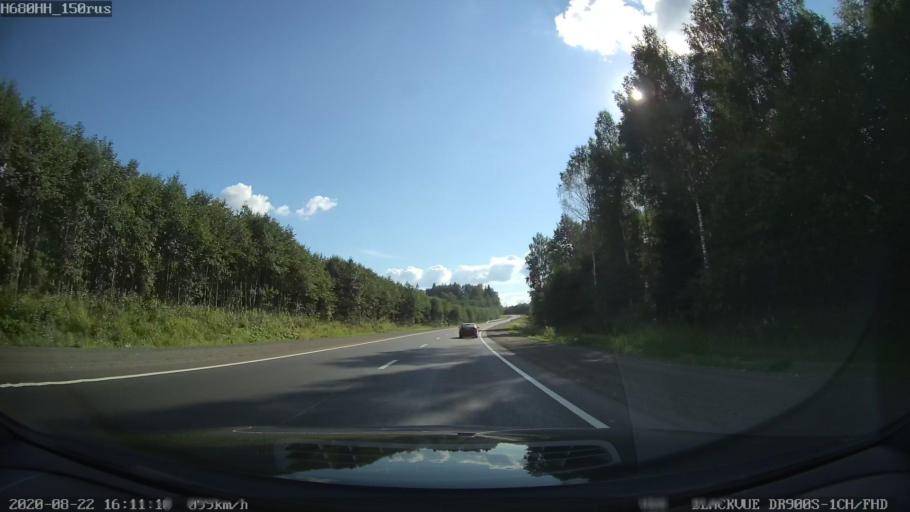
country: RU
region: Tverskaya
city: Rameshki
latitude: 57.5045
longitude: 36.2654
